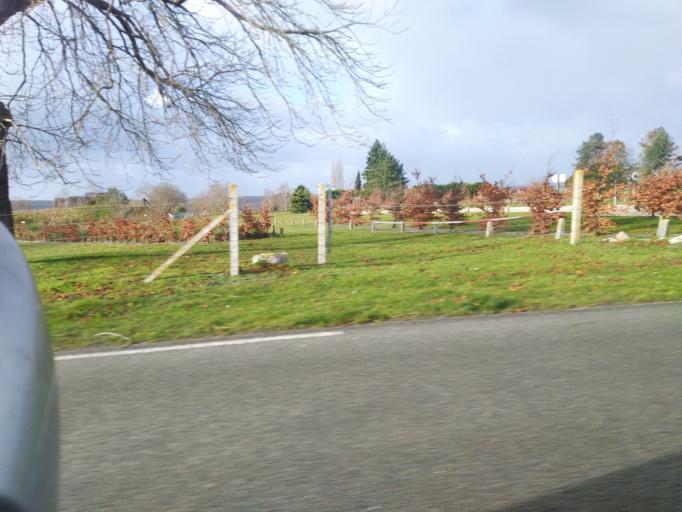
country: FR
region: Haute-Normandie
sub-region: Departement de la Seine-Maritime
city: Jumieges
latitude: 49.4415
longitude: 0.8260
